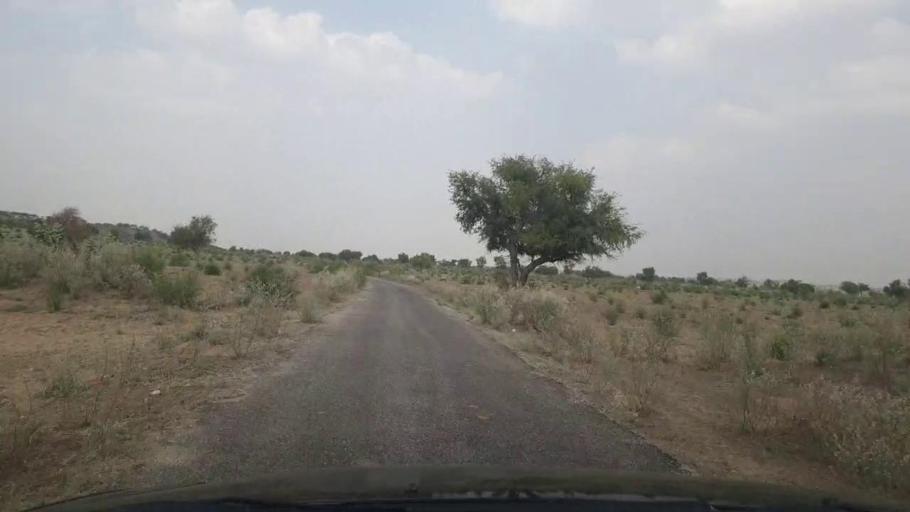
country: PK
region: Sindh
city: Islamkot
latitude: 24.9138
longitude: 70.5617
